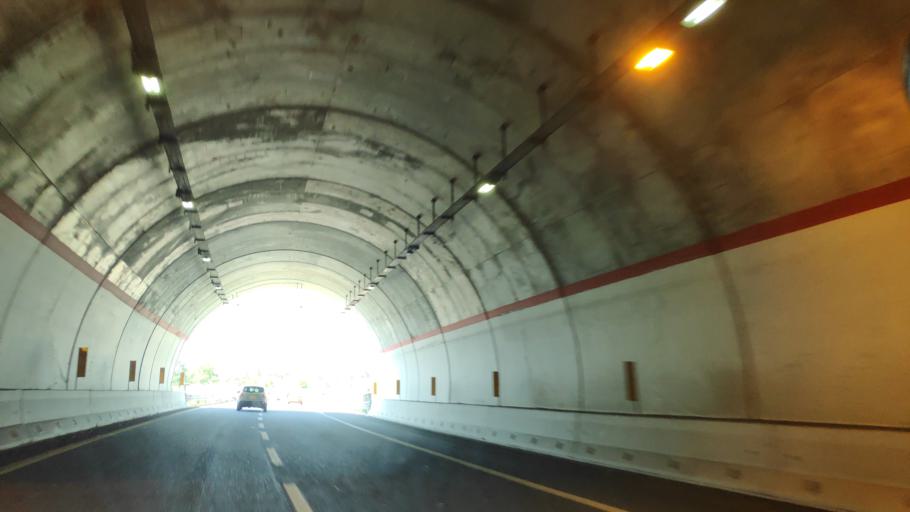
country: IT
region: Basilicate
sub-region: Provincia di Potenza
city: Nemoli
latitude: 40.0934
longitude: 15.8228
